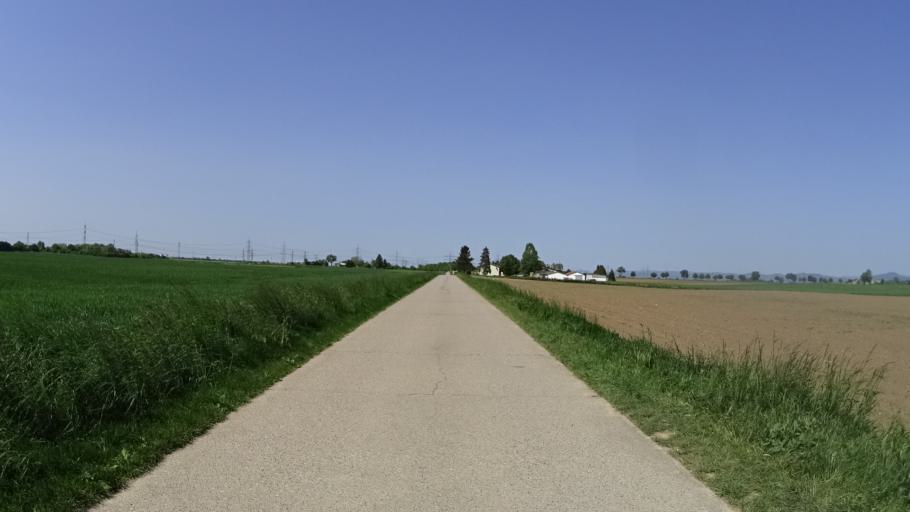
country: DE
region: Baden-Wuerttemberg
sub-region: Karlsruhe Region
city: Ilvesheim
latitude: 49.4847
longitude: 8.5684
